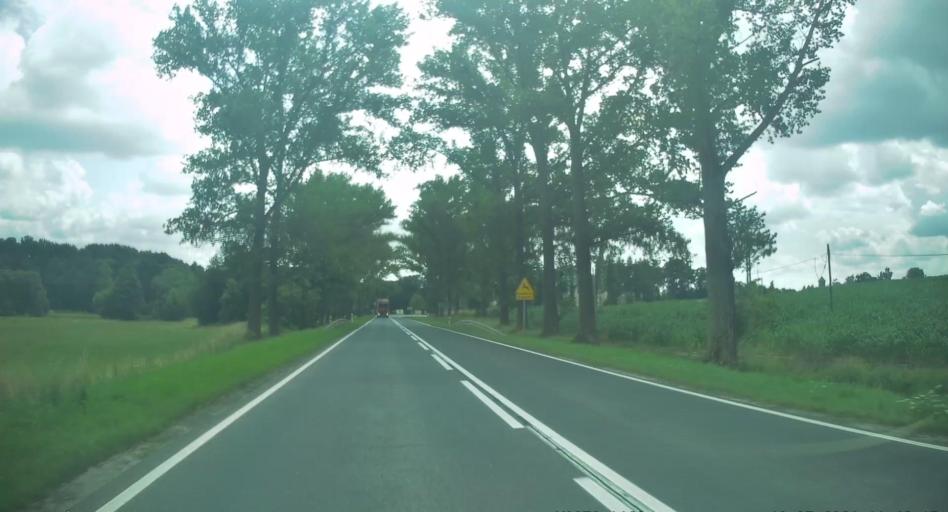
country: PL
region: Opole Voivodeship
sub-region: Powiat prudnicki
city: Laka Prudnicka
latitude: 50.3861
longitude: 17.5223
